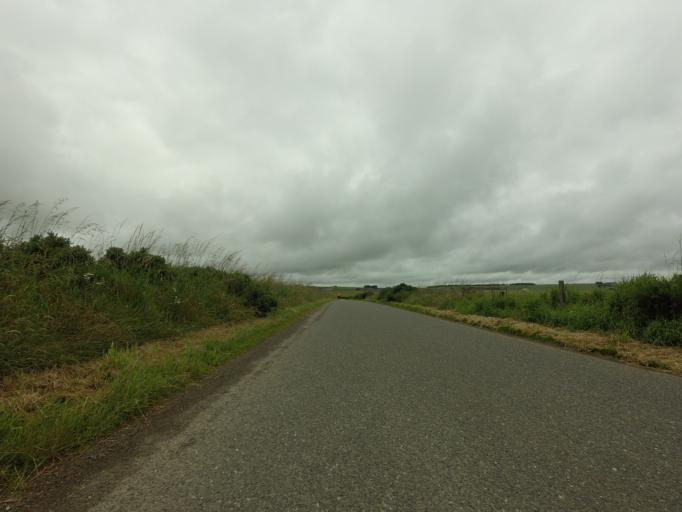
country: GB
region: Scotland
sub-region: Aberdeenshire
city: Turriff
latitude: 57.5446
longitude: -2.2935
